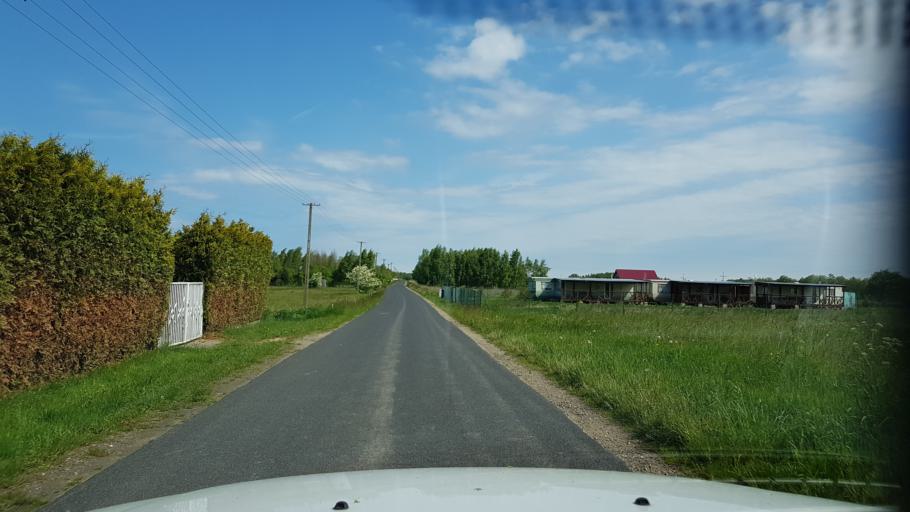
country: PL
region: West Pomeranian Voivodeship
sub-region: Powiat kolobrzeski
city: Ustronie Morskie
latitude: 54.2214
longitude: 15.8942
